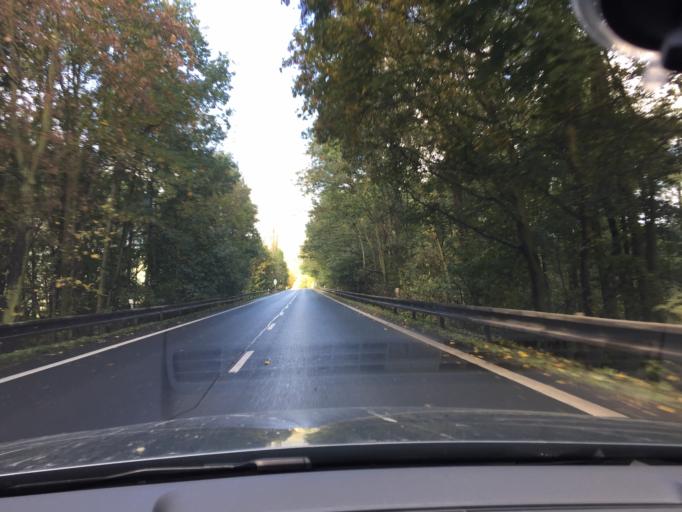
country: CZ
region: Ustecky
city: Chlumec
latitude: 50.6912
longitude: 13.9448
